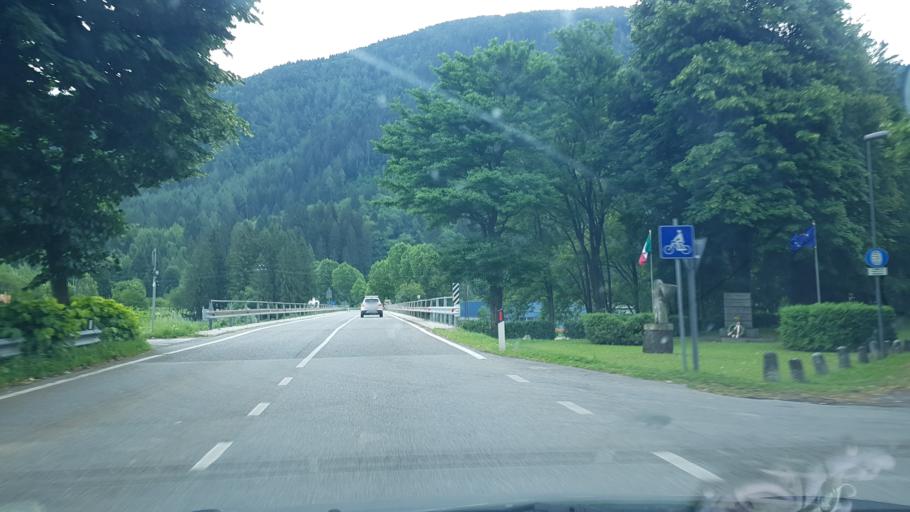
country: IT
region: Friuli Venezia Giulia
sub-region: Provincia di Udine
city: Sutrio
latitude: 46.5132
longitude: 12.9972
